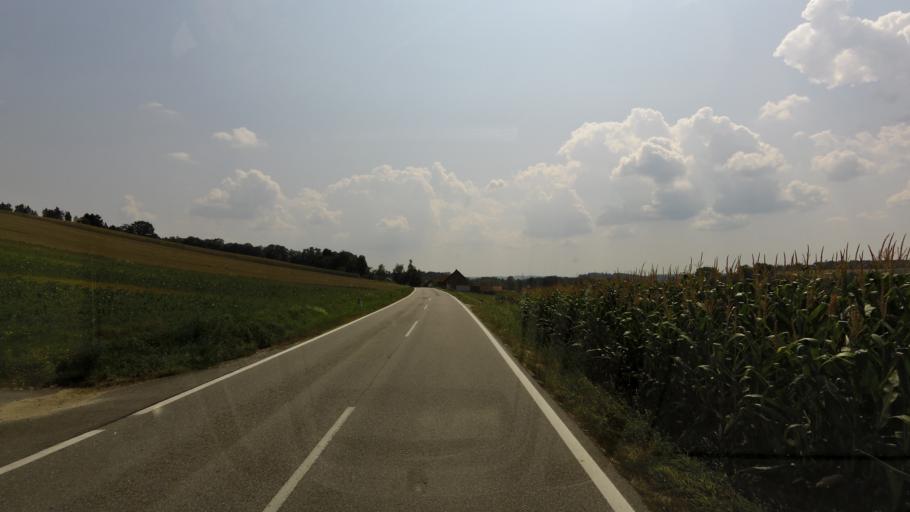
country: AT
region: Upper Austria
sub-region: Politischer Bezirk Ried im Innkreis
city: Waldzell
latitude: 48.1950
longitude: 13.3811
